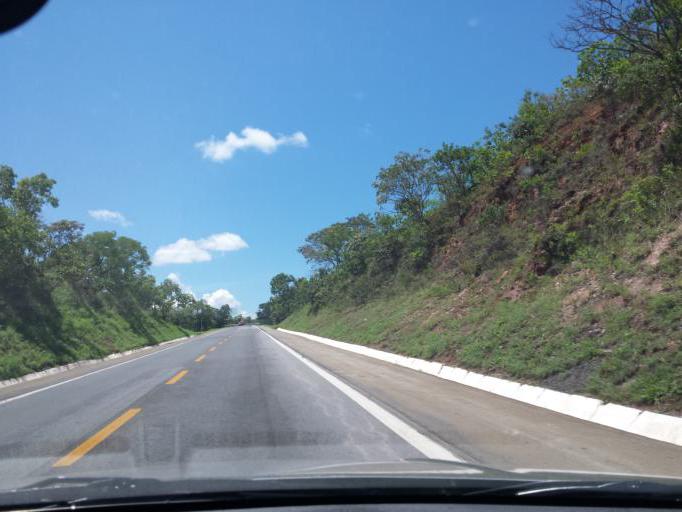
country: BR
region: Goias
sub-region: Luziania
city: Luziania
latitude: -16.4355
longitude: -47.8150
